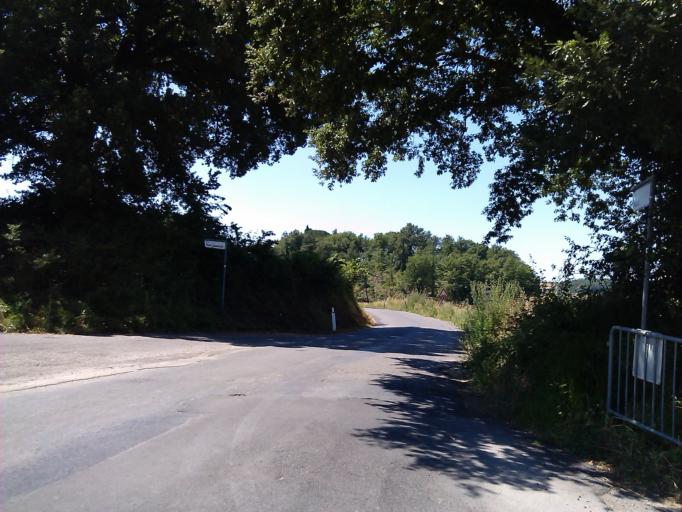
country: IT
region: Umbria
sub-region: Provincia di Terni
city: Fabro Scalo
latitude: 42.8608
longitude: 12.0468
